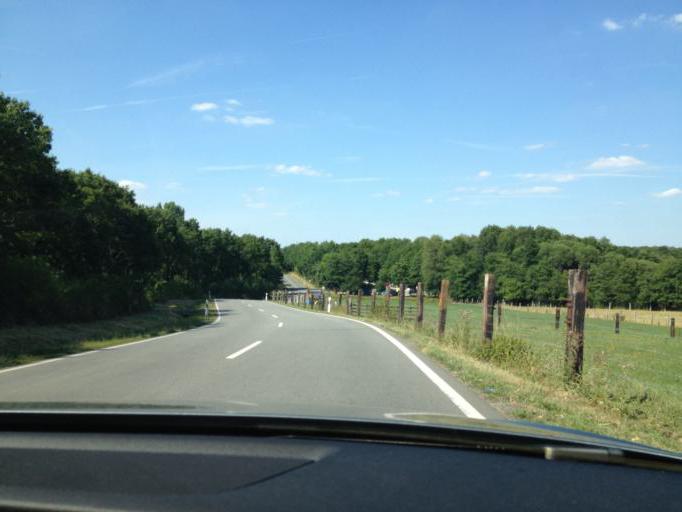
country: DE
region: Saarland
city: Oberthal
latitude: 49.5543
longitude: 7.0618
